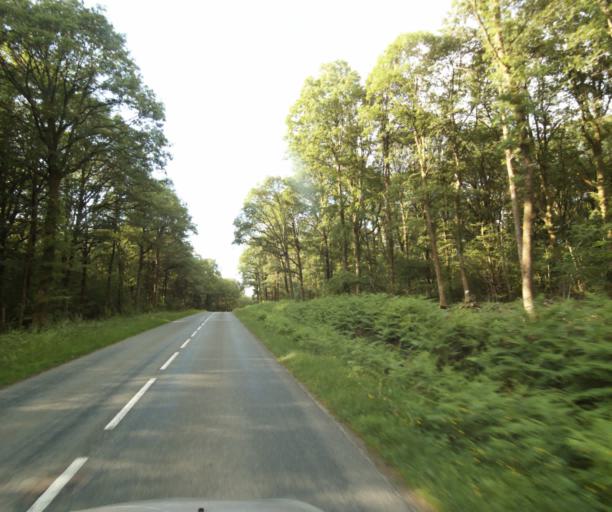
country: FR
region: Champagne-Ardenne
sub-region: Departement des Ardennes
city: Nouzonville
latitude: 49.8232
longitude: 4.6979
